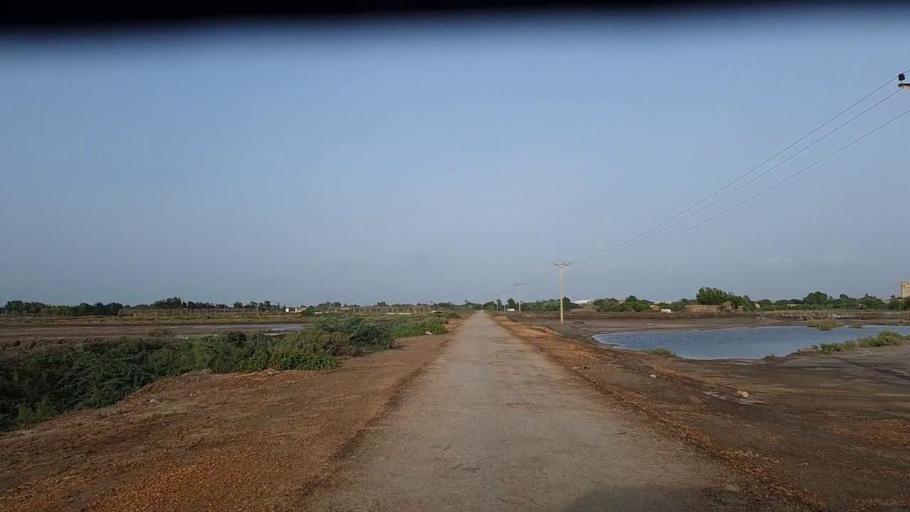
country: PK
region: Sindh
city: Thatta
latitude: 24.7601
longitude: 67.9094
